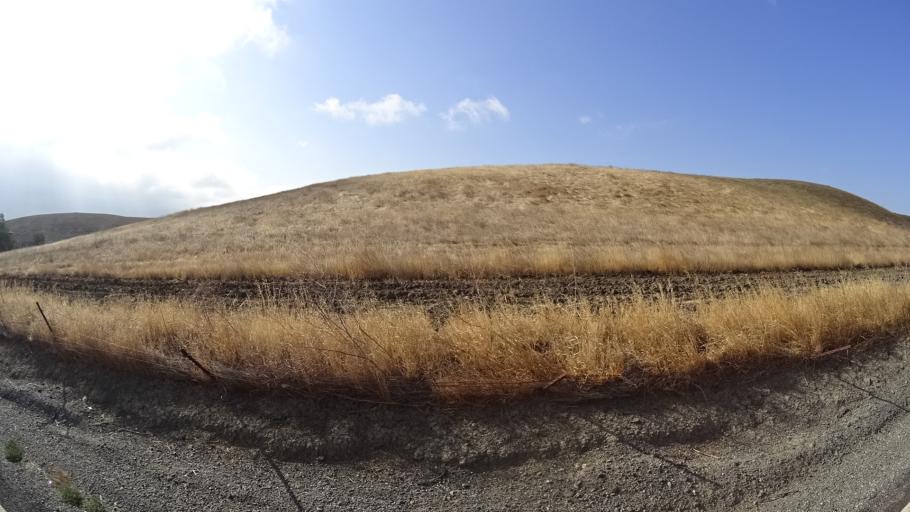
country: US
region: California
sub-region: Yolo County
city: Esparto
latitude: 38.7777
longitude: -121.9627
